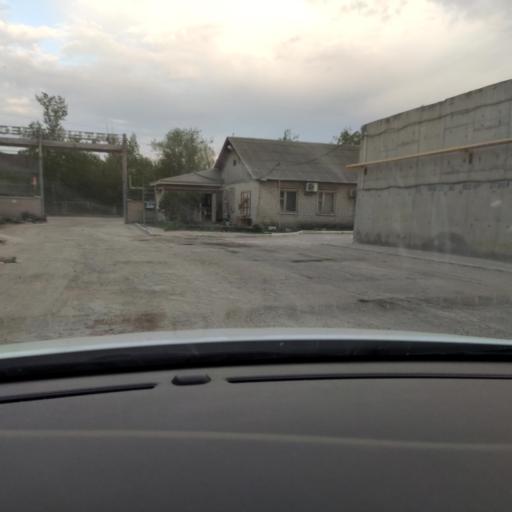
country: RU
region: Tatarstan
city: Verkhniy Uslon
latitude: 55.8027
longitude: 49.0457
